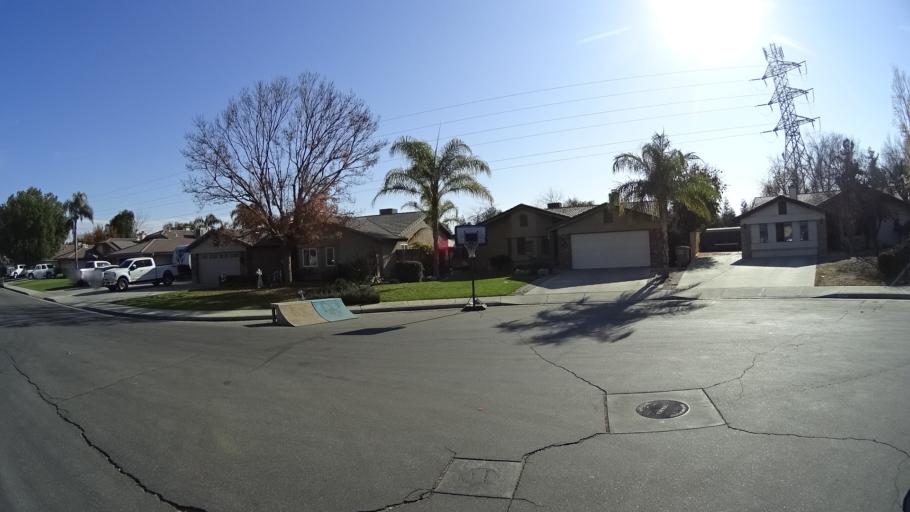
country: US
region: California
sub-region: Kern County
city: Greenacres
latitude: 35.3983
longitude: -119.0893
